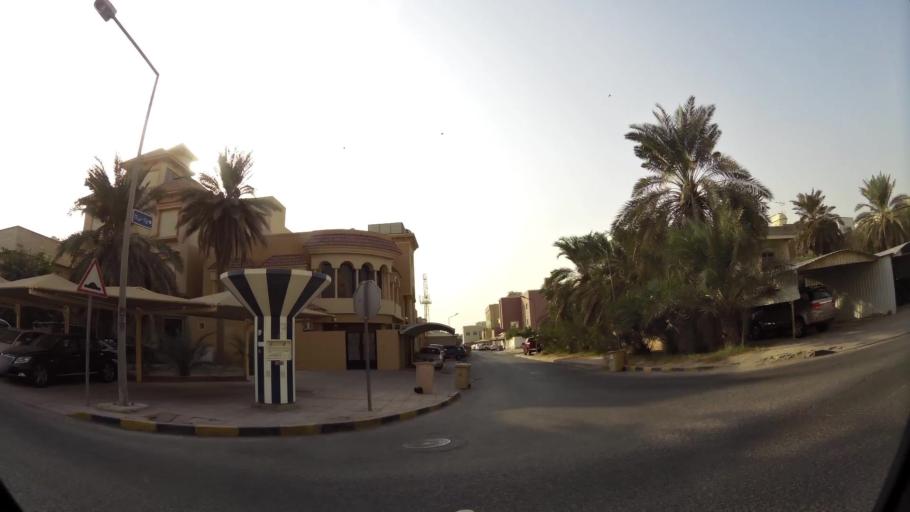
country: KW
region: Muhafazat Hawalli
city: As Salimiyah
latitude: 29.3226
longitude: 48.0826
